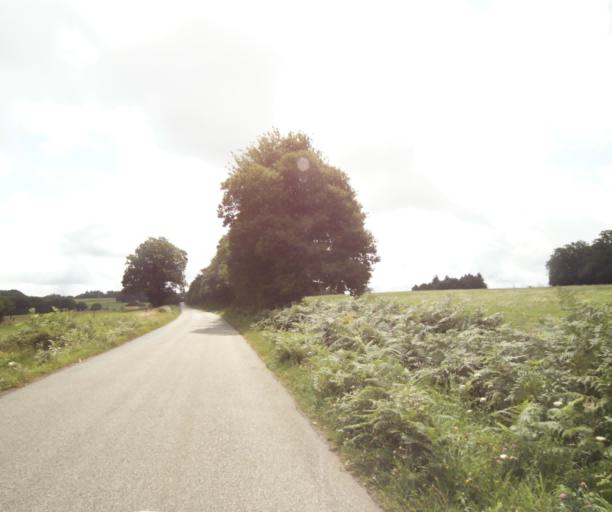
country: FR
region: Limousin
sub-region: Departement de la Correze
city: Sainte-Fortunade
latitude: 45.1958
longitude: 1.7996
